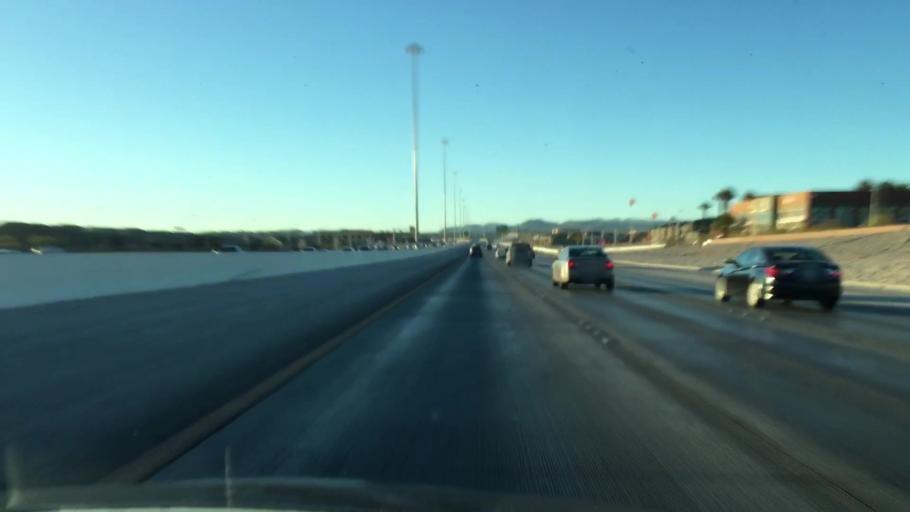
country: US
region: Nevada
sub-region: Clark County
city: Spring Valley
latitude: 36.0838
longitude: -115.2890
